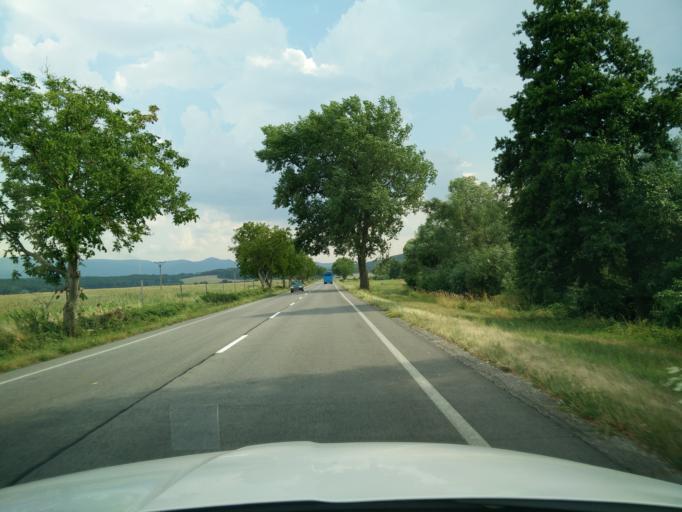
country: SK
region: Nitriansky
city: Novaky
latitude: 48.7415
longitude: 18.5014
